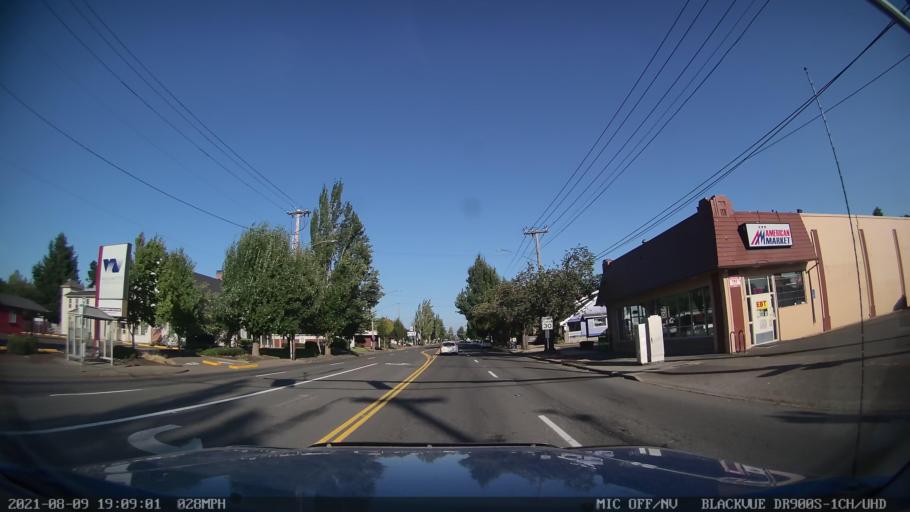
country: US
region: Oregon
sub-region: Marion County
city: Salem
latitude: 44.9362
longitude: -123.0243
